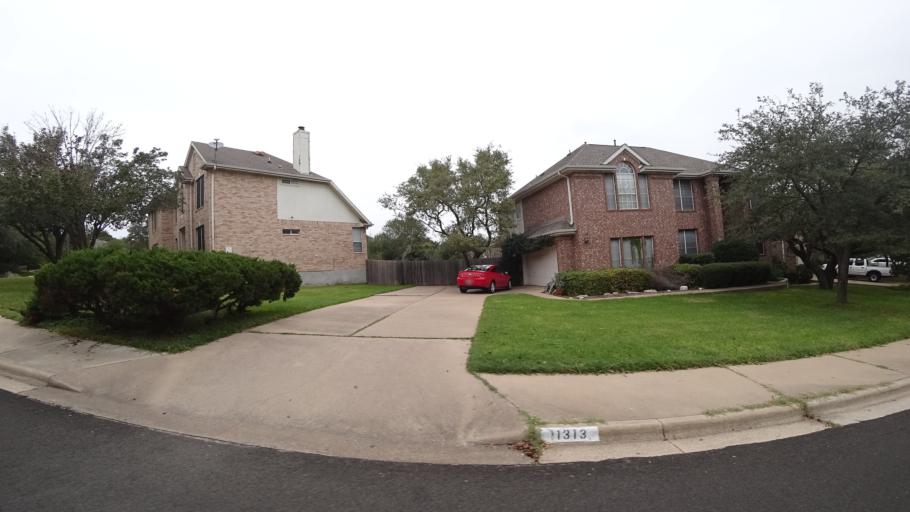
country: US
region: Texas
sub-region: Travis County
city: Shady Hollow
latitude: 30.1824
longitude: -97.8908
